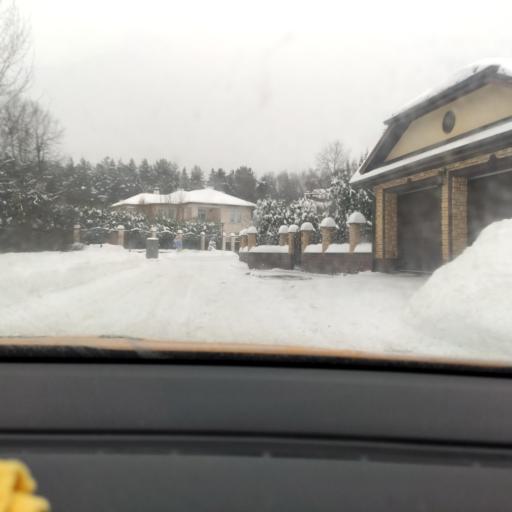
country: RU
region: Moskovskaya
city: Zarech'ye
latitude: 55.6742
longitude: 37.3924
